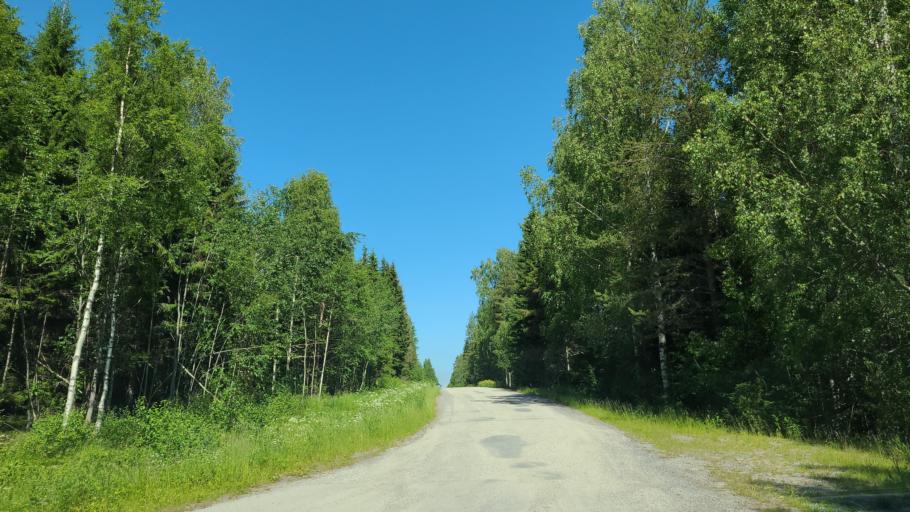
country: SE
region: Vaesternorrland
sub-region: OErnskoeldsviks Kommun
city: Husum
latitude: 63.4153
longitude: 19.2203
